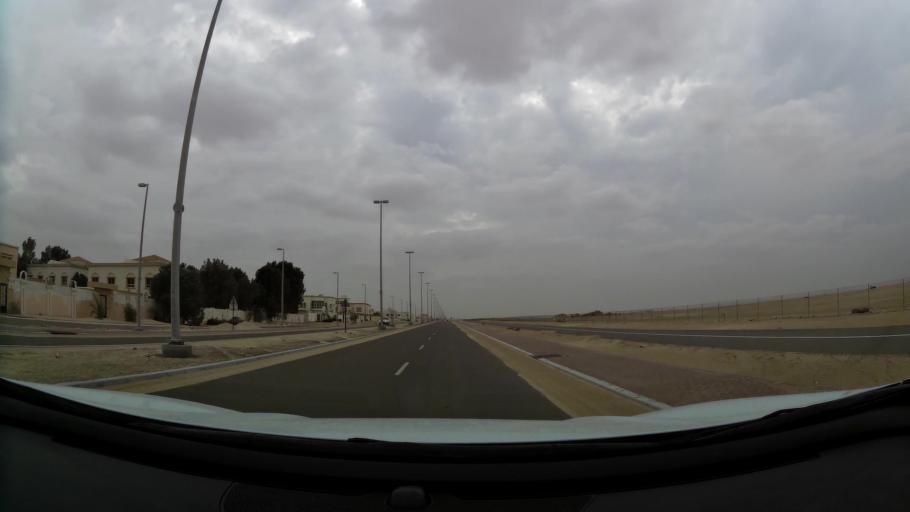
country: AE
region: Abu Dhabi
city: Abu Dhabi
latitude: 24.3751
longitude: 54.6284
